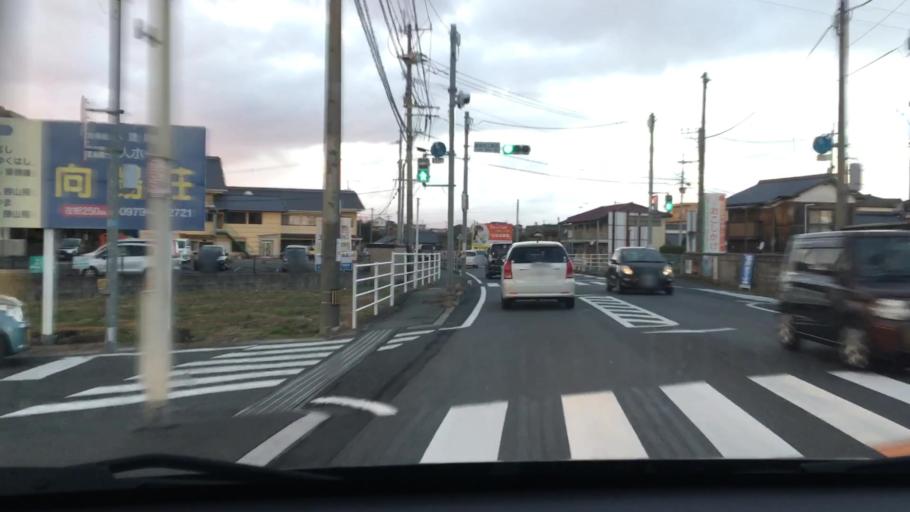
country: JP
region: Fukuoka
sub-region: Buzen-shi
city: Buzen
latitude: 33.6220
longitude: 131.0945
